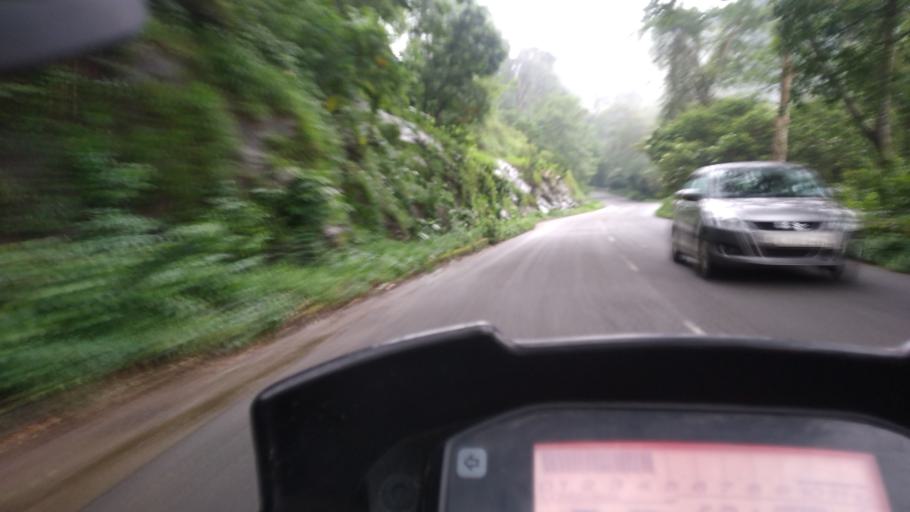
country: IN
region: Kerala
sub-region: Idukki
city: Kuttampuzha
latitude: 10.0645
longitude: 76.7892
